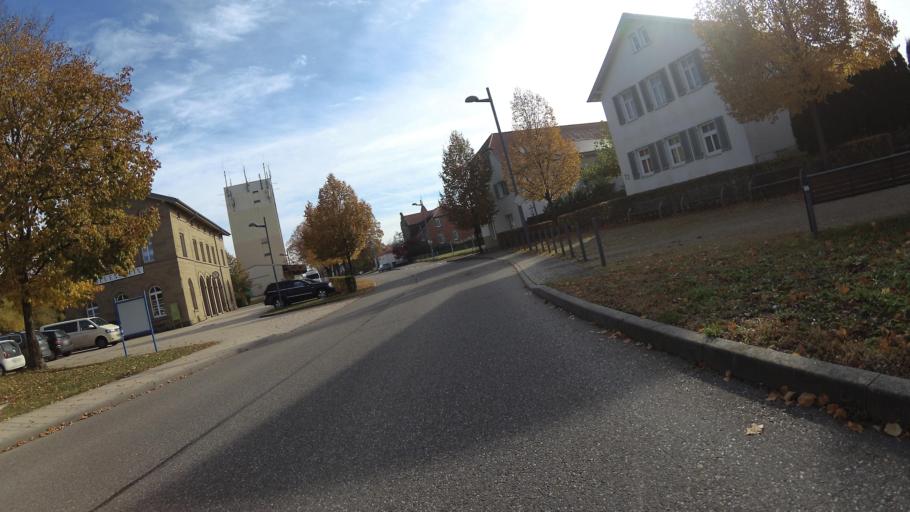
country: DE
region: Baden-Wuerttemberg
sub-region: Regierungsbezirk Stuttgart
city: Neuenstein
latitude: 49.2058
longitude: 9.5847
